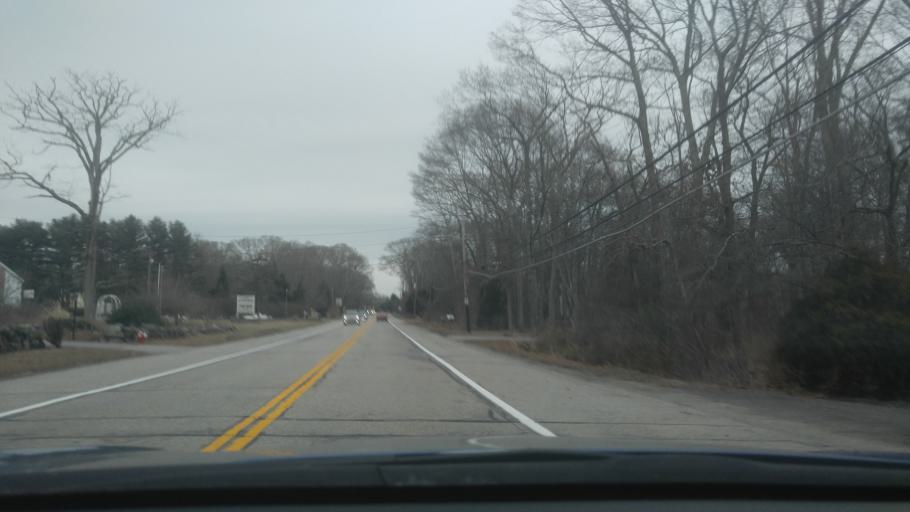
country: US
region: Rhode Island
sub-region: Washington County
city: North Kingstown
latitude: 41.5591
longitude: -71.4441
